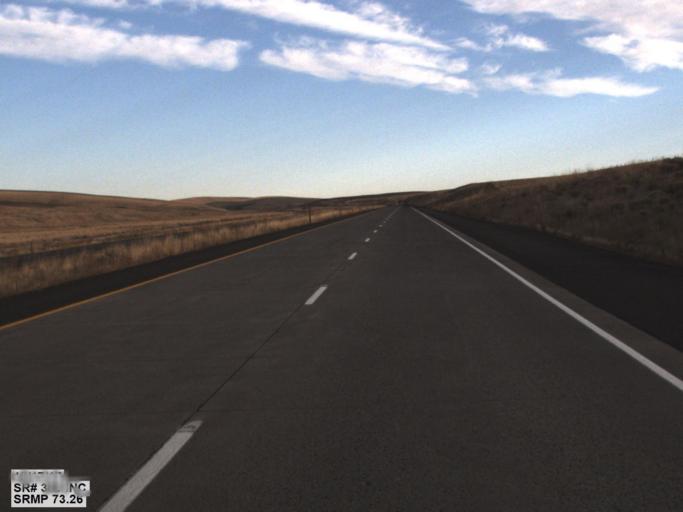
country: US
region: Washington
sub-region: Franklin County
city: Connell
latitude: 46.8519
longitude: -118.6390
